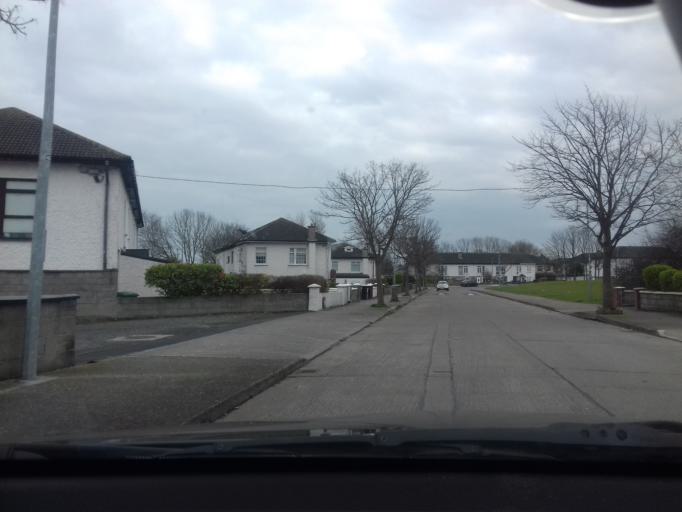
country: IE
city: Bayside
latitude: 53.3947
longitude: -6.1387
